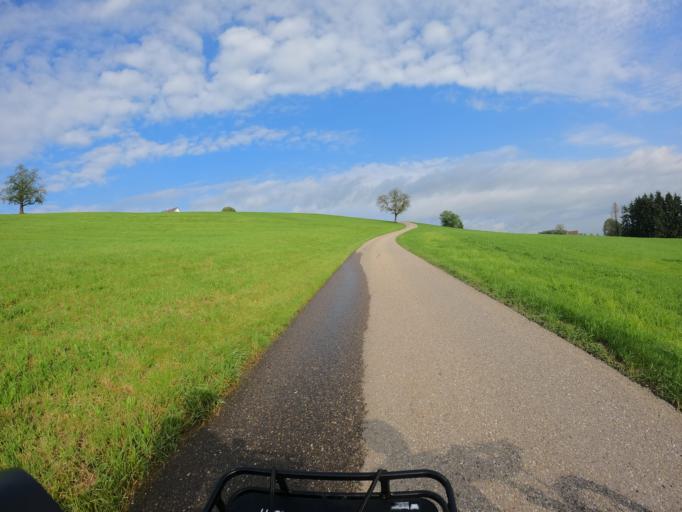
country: CH
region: Aargau
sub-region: Bezirk Muri
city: Buttwil
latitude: 47.2338
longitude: 8.3236
